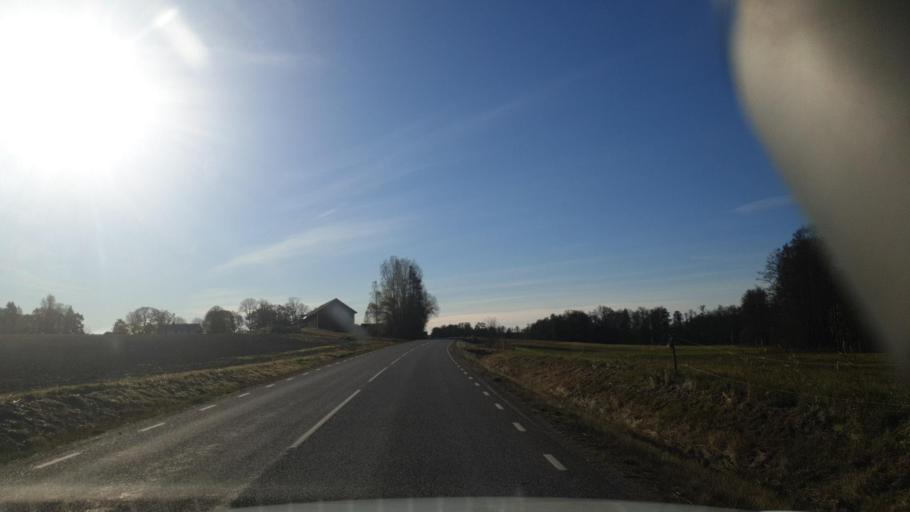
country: SE
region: Vaermland
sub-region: Grums Kommun
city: Grums
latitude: 59.3997
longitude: 13.0705
